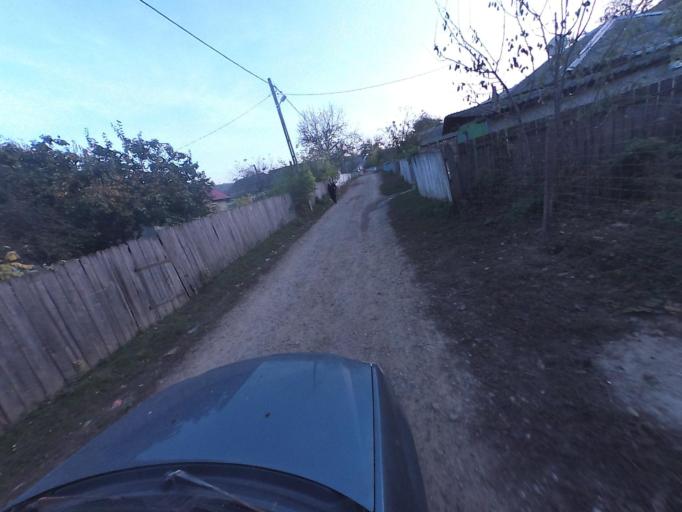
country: RO
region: Vaslui
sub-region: Comuna Garceni
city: Garceni
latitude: 46.7874
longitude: 27.2439
